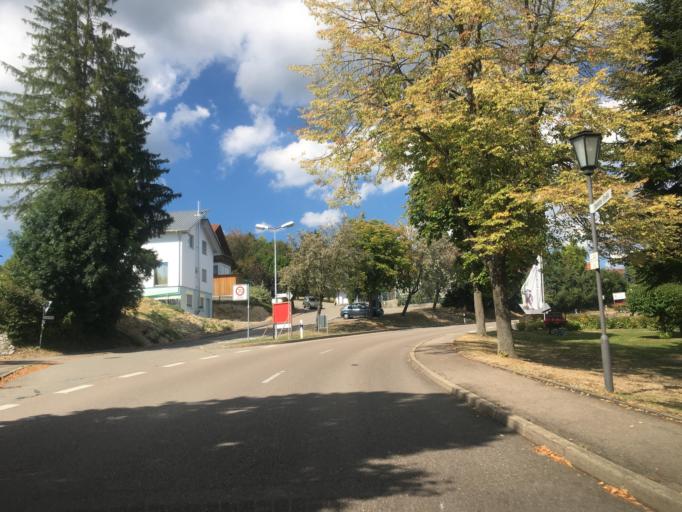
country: DE
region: Baden-Wuerttemberg
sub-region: Tuebingen Region
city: Hayingen
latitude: 48.2770
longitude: 9.4736
